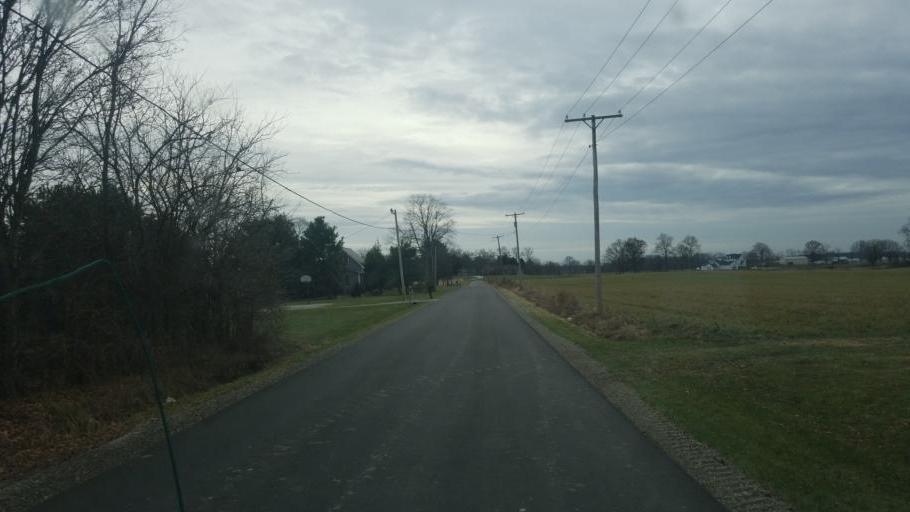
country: US
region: Ohio
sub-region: Morrow County
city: Cardington
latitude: 40.4712
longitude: -82.8961
